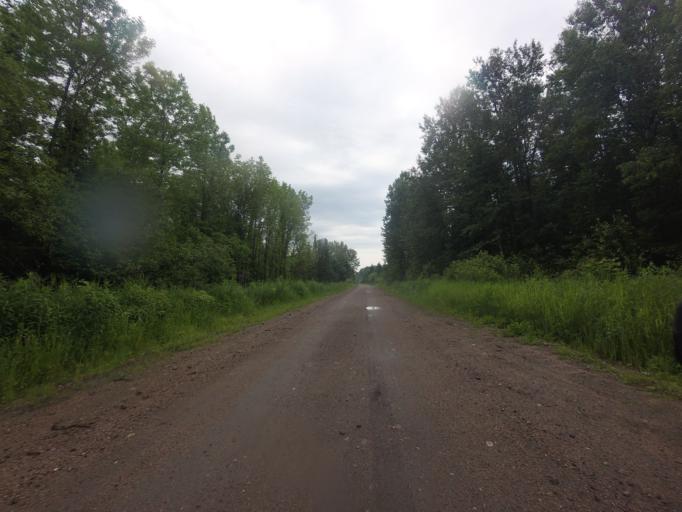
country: CA
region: Quebec
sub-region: Outaouais
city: Maniwaki
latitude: 46.3434
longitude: -76.0003
